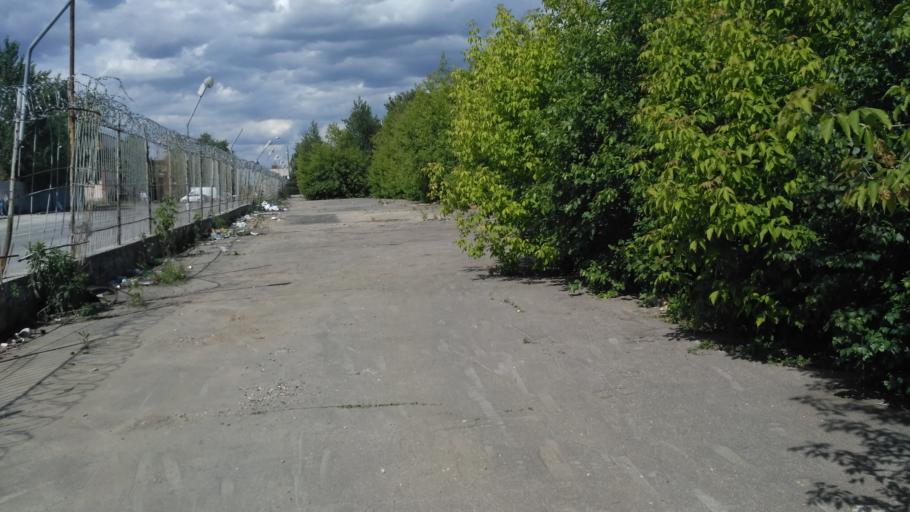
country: RU
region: Moscow
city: Kozeyevo
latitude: 55.8857
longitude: 37.6346
